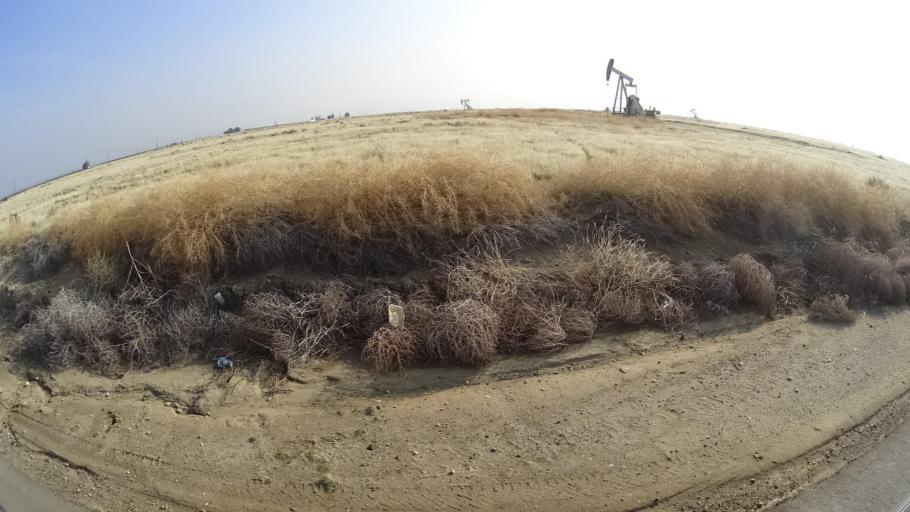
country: US
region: California
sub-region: Kern County
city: Lebec
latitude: 34.9905
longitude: -118.9087
